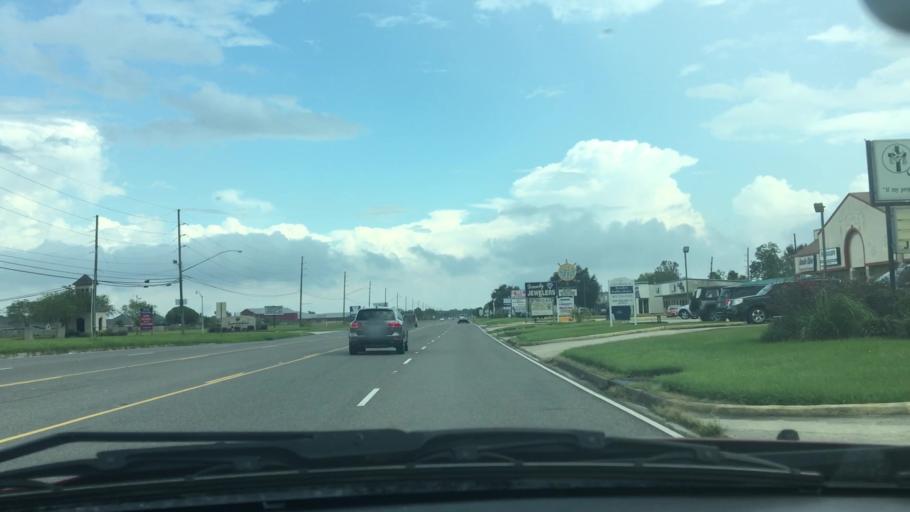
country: US
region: Louisiana
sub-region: Saint John the Baptist Parish
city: Laplace
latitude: 30.0752
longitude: -90.4726
